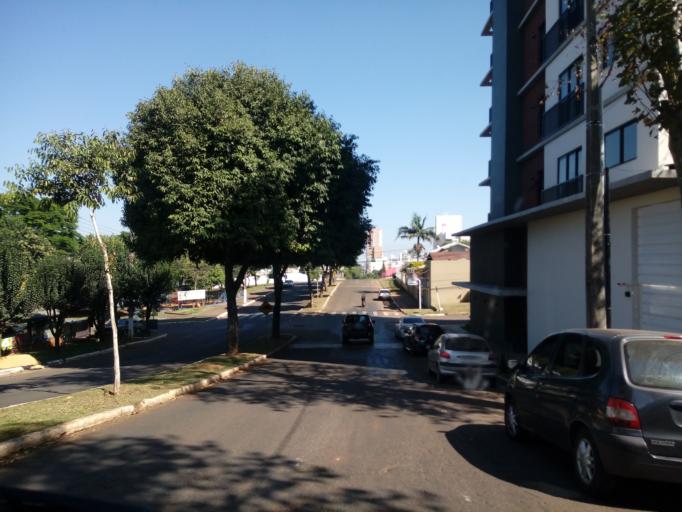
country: BR
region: Santa Catarina
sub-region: Chapeco
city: Chapeco
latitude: -27.0916
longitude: -52.6001
